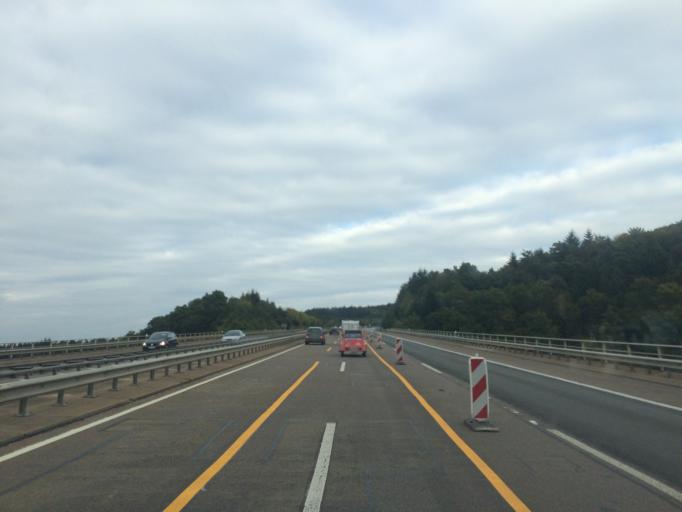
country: DE
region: Rheinland-Pfalz
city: Mehring
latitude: 49.7837
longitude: 6.8088
